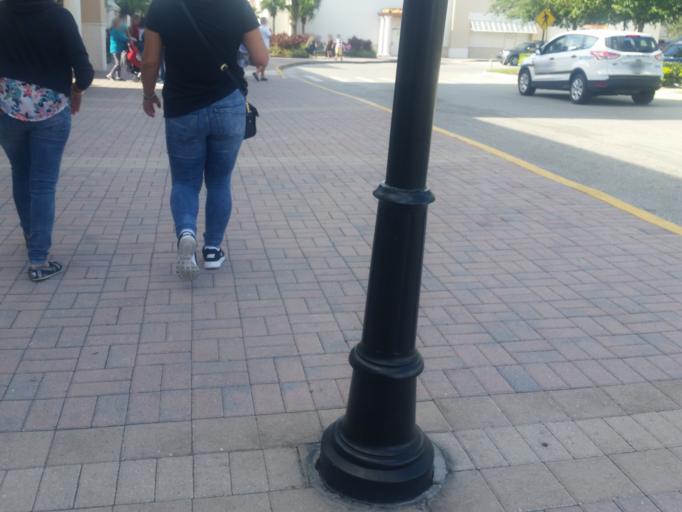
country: US
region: Florida
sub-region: Orange County
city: Tangelo Park
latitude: 28.4734
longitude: -81.4514
